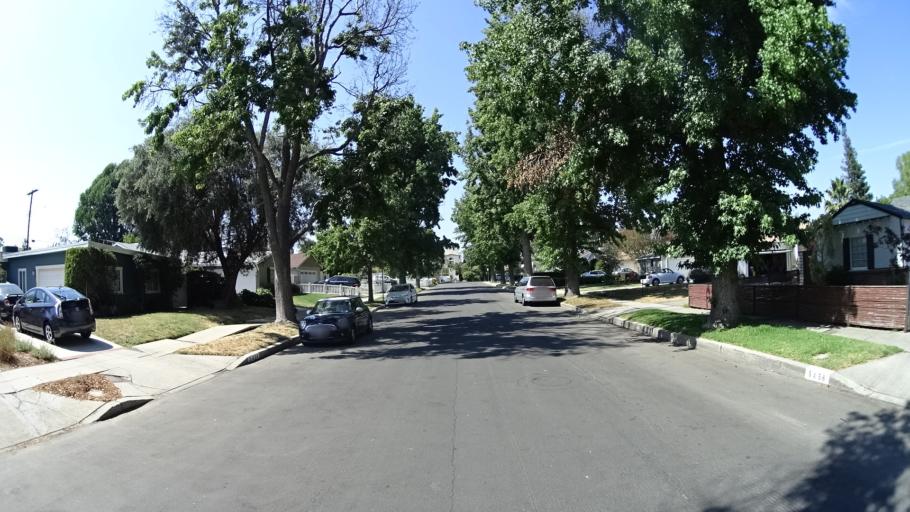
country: US
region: California
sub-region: Los Angeles County
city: Van Nuys
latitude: 34.1701
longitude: -118.4640
